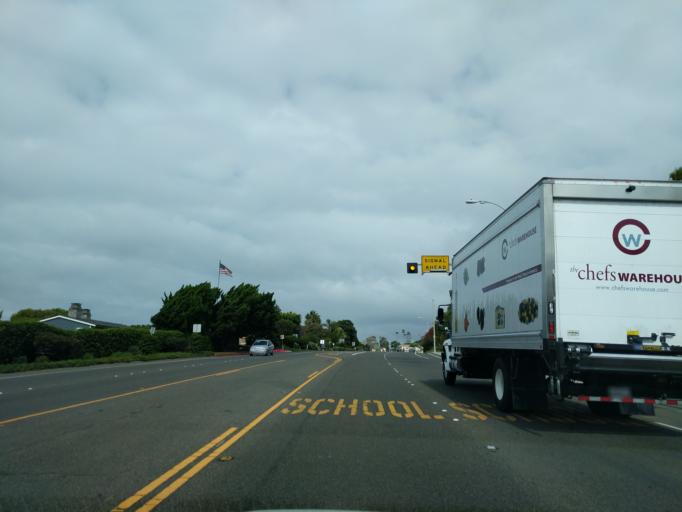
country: US
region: California
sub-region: Orange County
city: Laguna Beach
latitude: 33.5185
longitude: -117.7595
